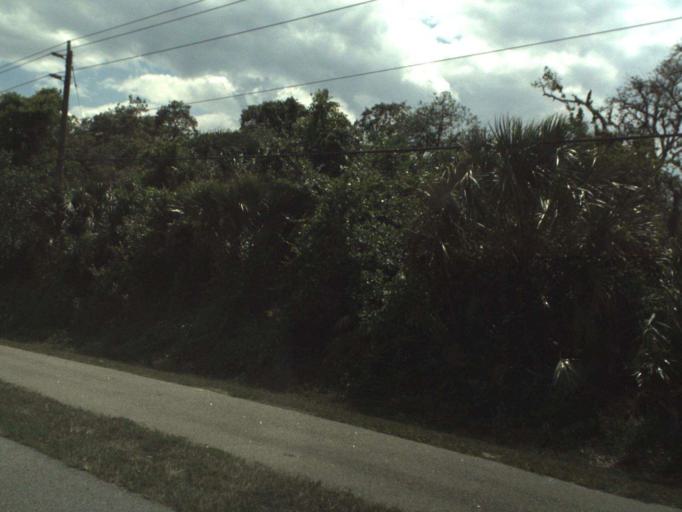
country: US
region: Florida
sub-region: Brevard County
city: Titusville
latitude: 28.5913
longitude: -80.8470
